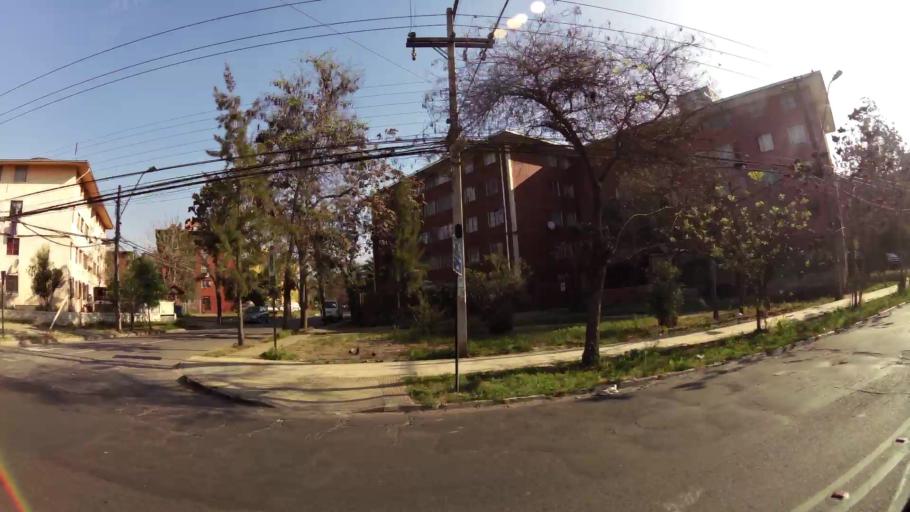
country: CL
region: Santiago Metropolitan
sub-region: Provincia de Santiago
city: Santiago
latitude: -33.4198
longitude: -70.6704
